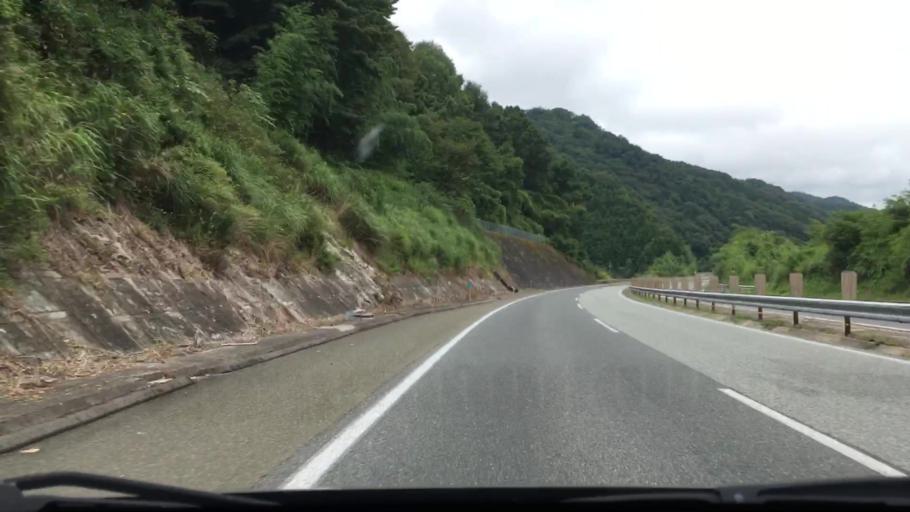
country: JP
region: Hiroshima
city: Shobara
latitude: 34.8383
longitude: 133.0824
